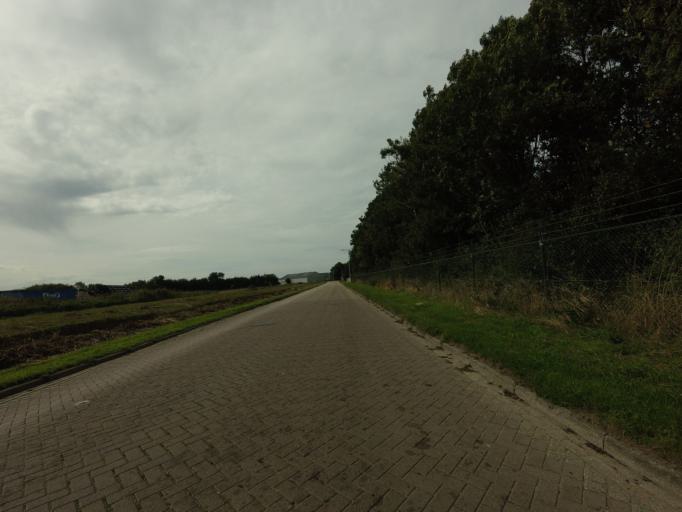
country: NL
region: North Holland
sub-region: Gemeente Texel
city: Den Burg
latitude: 53.0451
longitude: 4.8534
